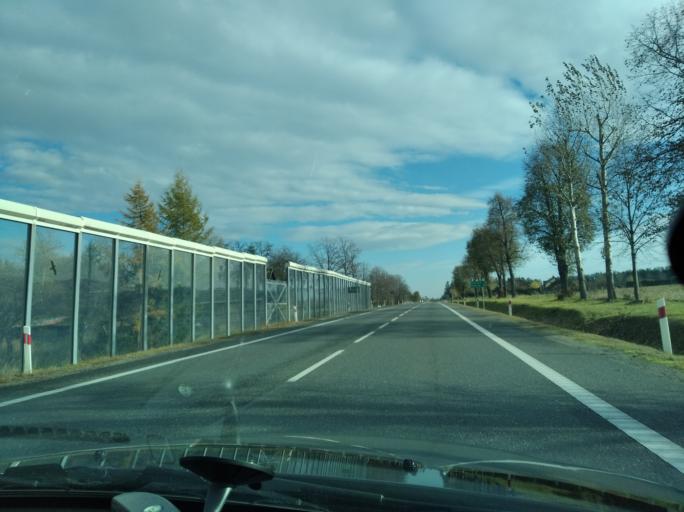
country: PL
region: Subcarpathian Voivodeship
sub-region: Powiat debicki
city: Brzeznica
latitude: 50.0612
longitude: 21.4963
